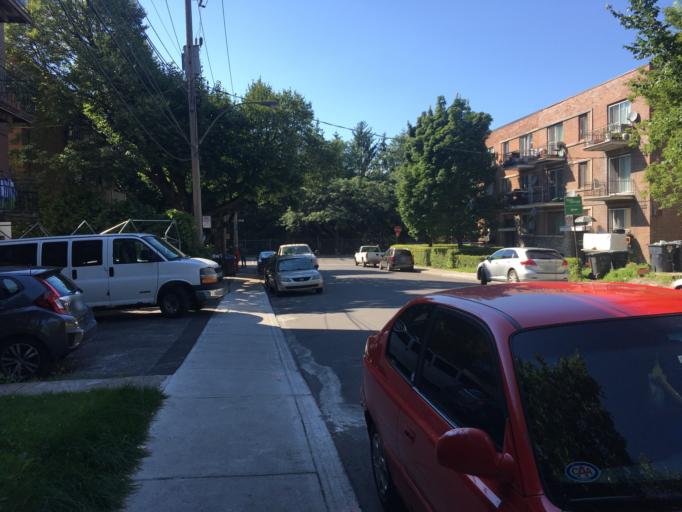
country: CA
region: Quebec
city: Mont-Royal
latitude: 45.5060
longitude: -73.6345
